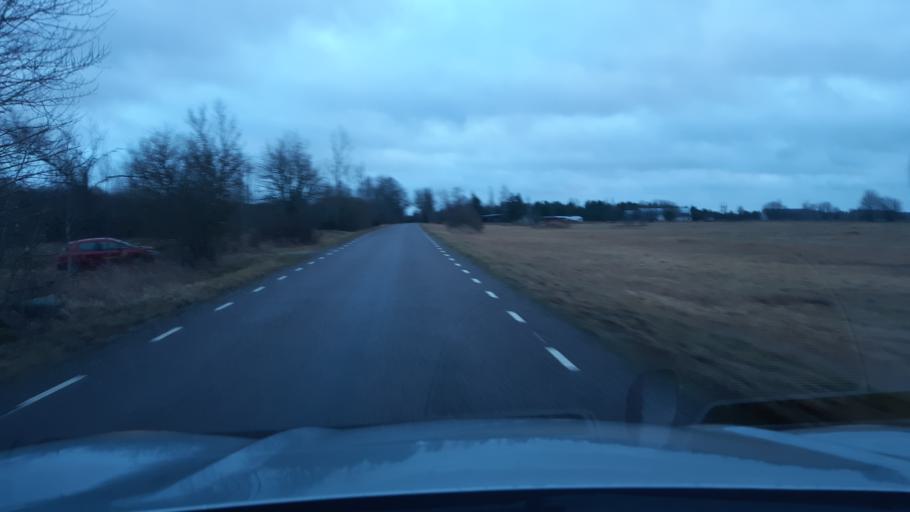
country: EE
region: Raplamaa
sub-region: Rapla vald
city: Rapla
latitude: 58.9895
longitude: 24.7271
